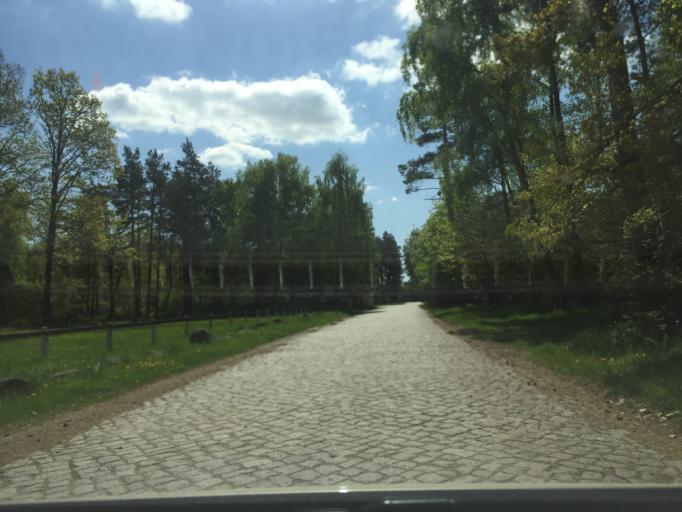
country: DE
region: Mecklenburg-Vorpommern
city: Torgelow
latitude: 53.6281
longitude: 13.9871
